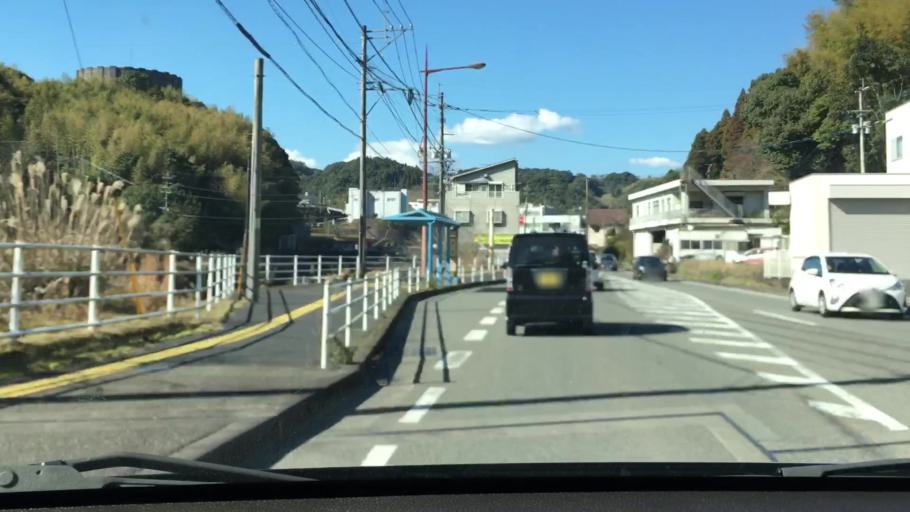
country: JP
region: Kagoshima
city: Kagoshima-shi
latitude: 31.6391
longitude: 130.5184
